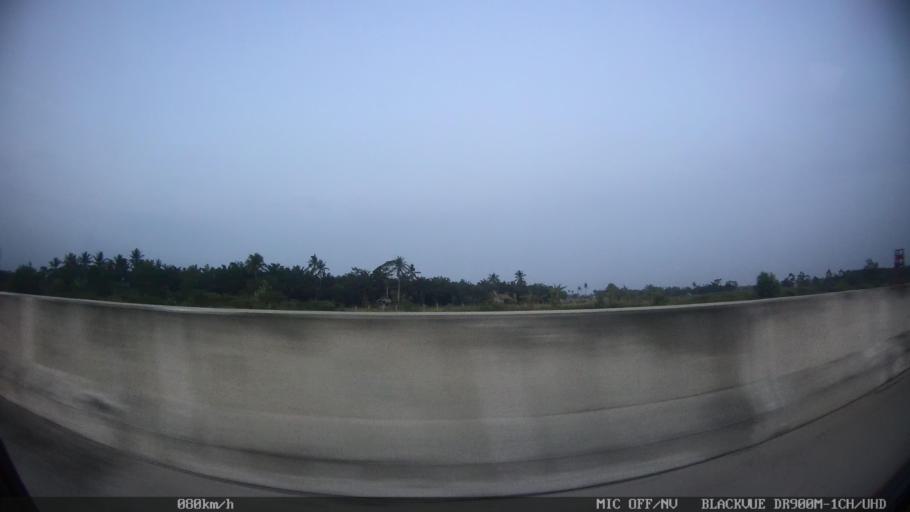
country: ID
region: Lampung
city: Sidorejo
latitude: -5.6240
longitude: 105.5640
